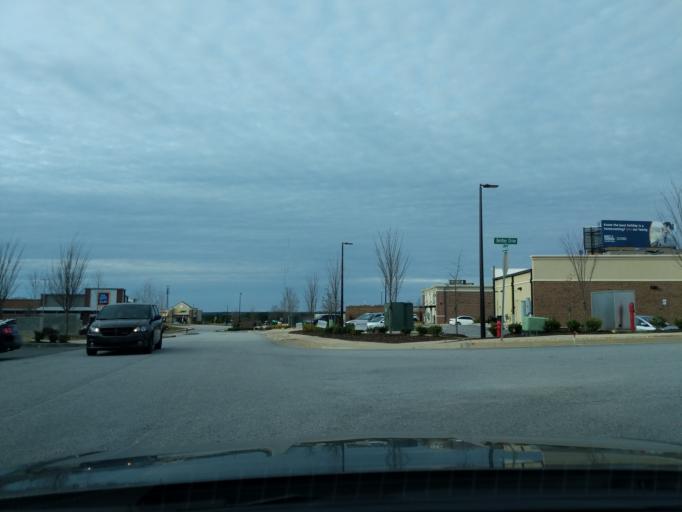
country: US
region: Georgia
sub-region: Columbia County
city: Grovetown
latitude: 33.4772
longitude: -82.1984
